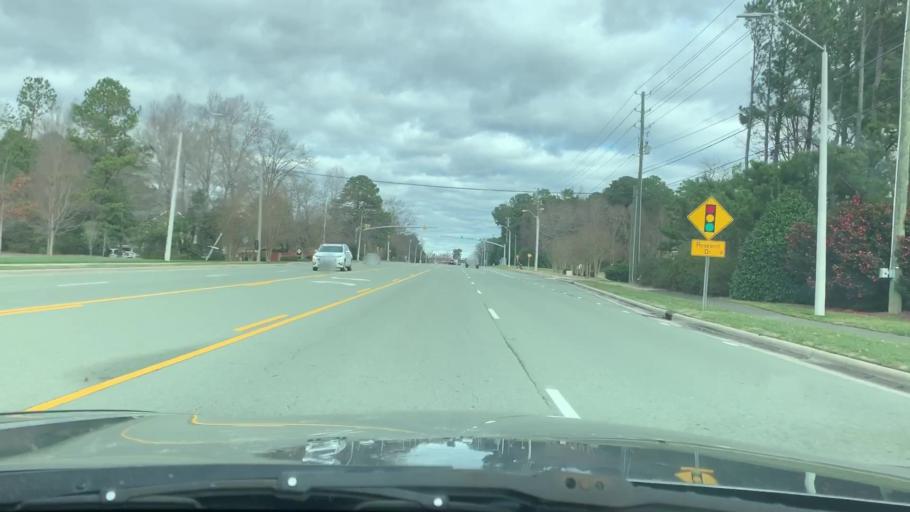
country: US
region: North Carolina
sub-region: Wake County
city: Cary
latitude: 35.8211
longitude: -78.7710
